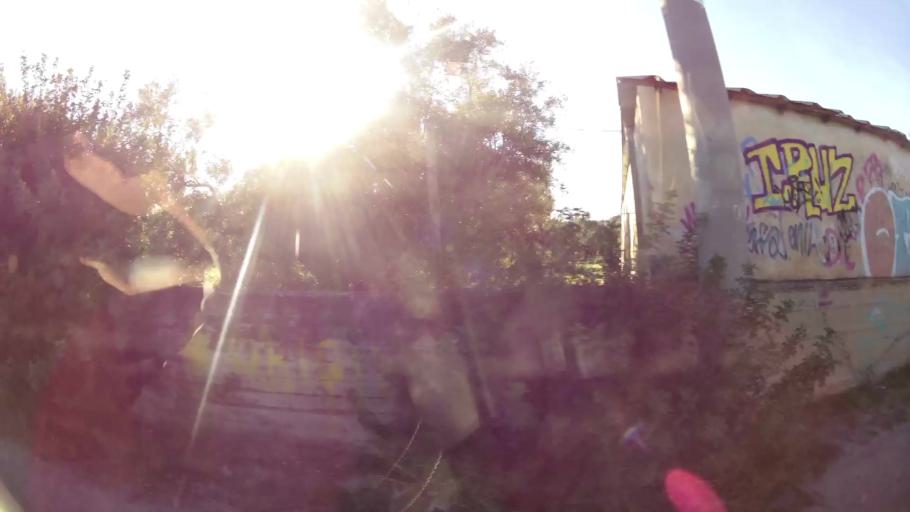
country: GR
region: Attica
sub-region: Nomarchia Anatolikis Attikis
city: Vari
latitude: 37.8281
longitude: 23.8059
